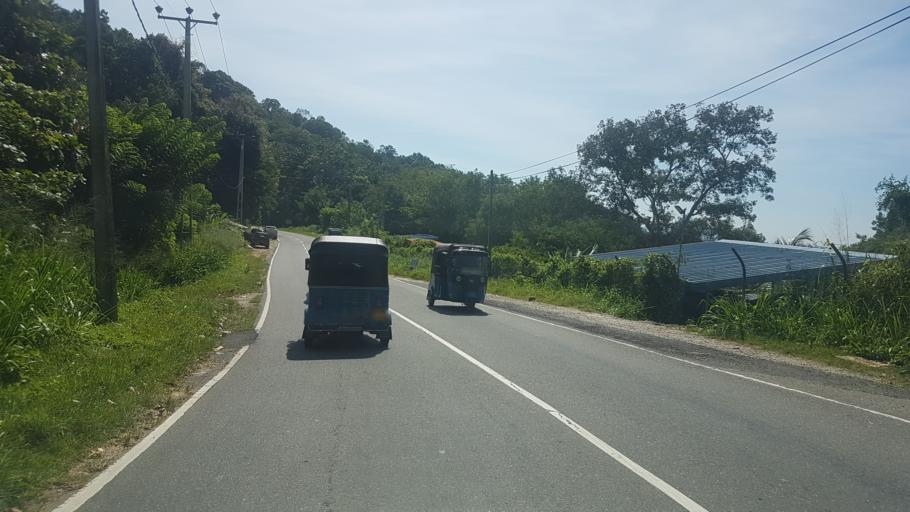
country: LK
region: Uva
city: Haputale
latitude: 6.8054
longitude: 81.0851
